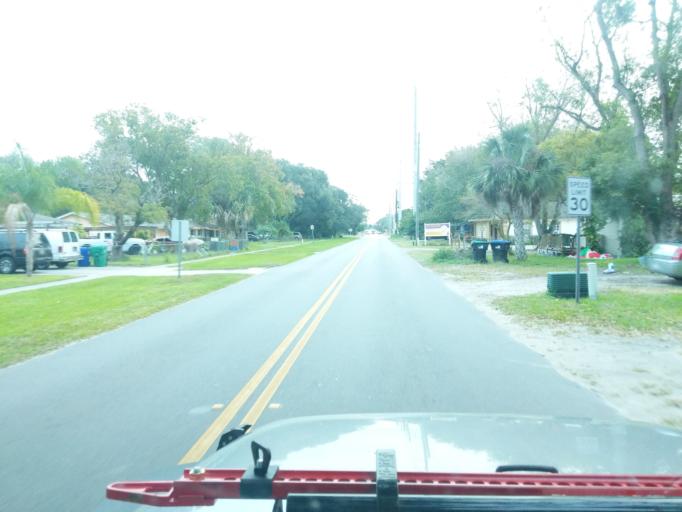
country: US
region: Florida
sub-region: Orange County
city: Winter Garden
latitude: 28.5584
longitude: -81.5792
